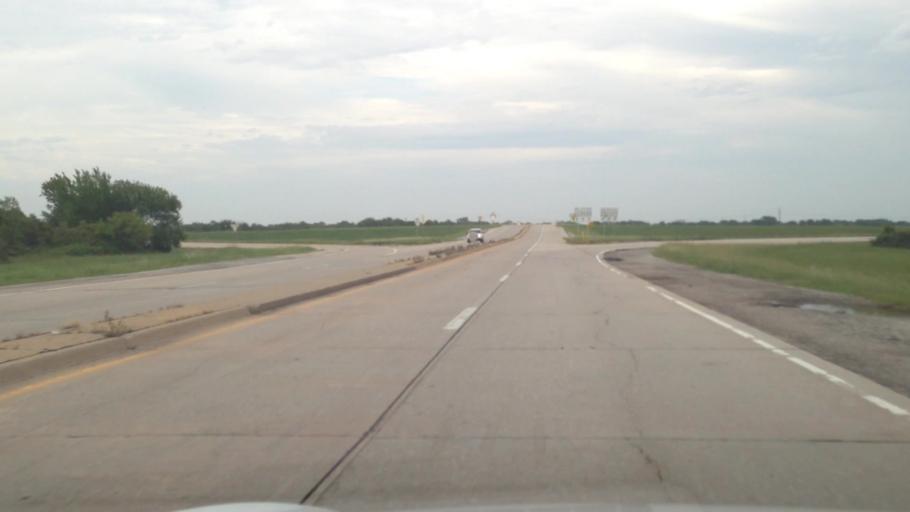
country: US
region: Oklahoma
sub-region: Ottawa County
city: Afton
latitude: 36.7185
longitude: -94.9317
